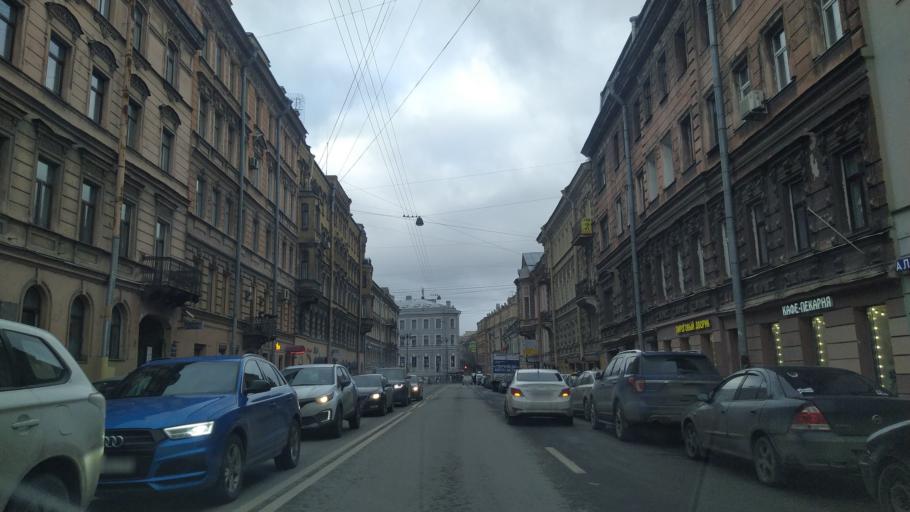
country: RU
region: St.-Petersburg
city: Centralniy
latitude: 59.9254
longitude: 30.3444
